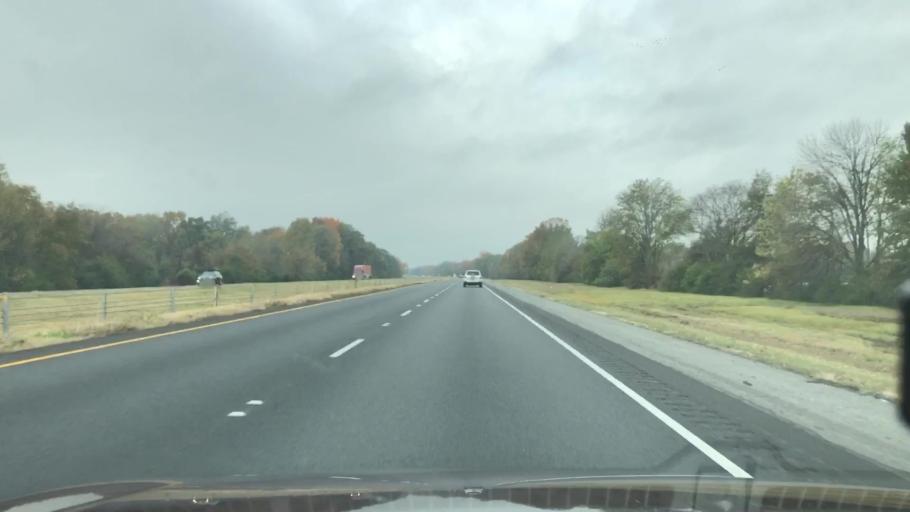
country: US
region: Louisiana
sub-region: Richland Parish
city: Rayville
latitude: 32.4648
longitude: -91.7952
